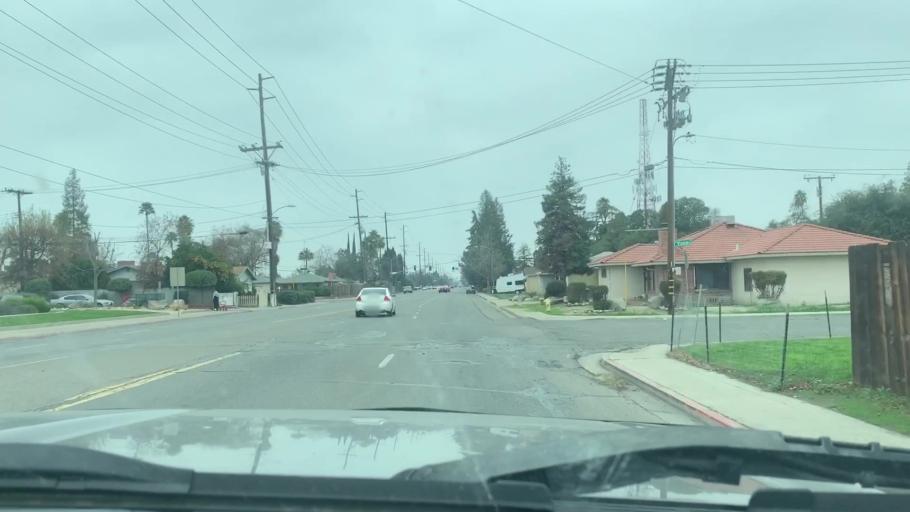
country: US
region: California
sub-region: Tulare County
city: Visalia
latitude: 36.3130
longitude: -119.3166
